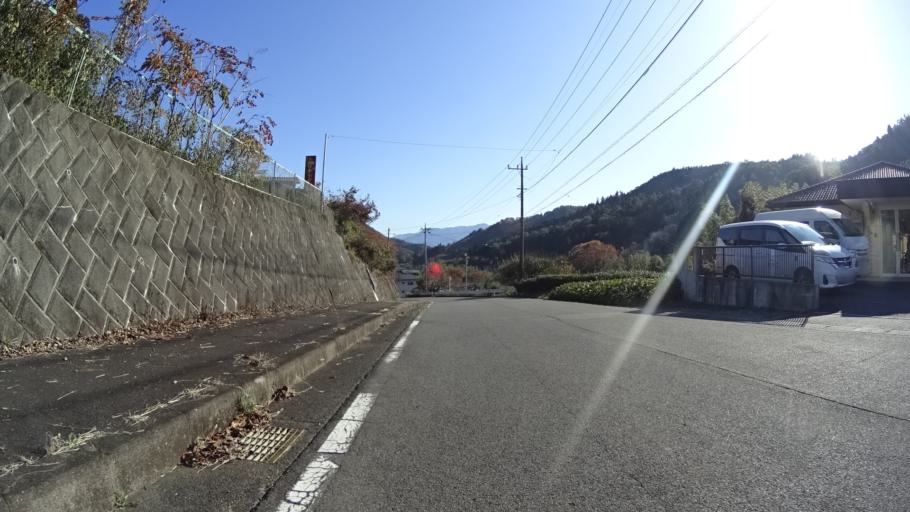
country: JP
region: Yamanashi
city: Uenohara
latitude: 35.6504
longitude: 139.1215
